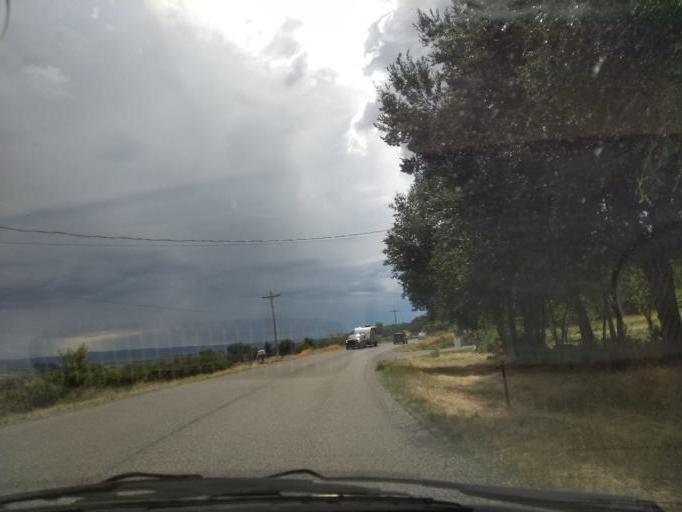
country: US
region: Colorado
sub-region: Delta County
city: Paonia
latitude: 38.8822
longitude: -107.5924
